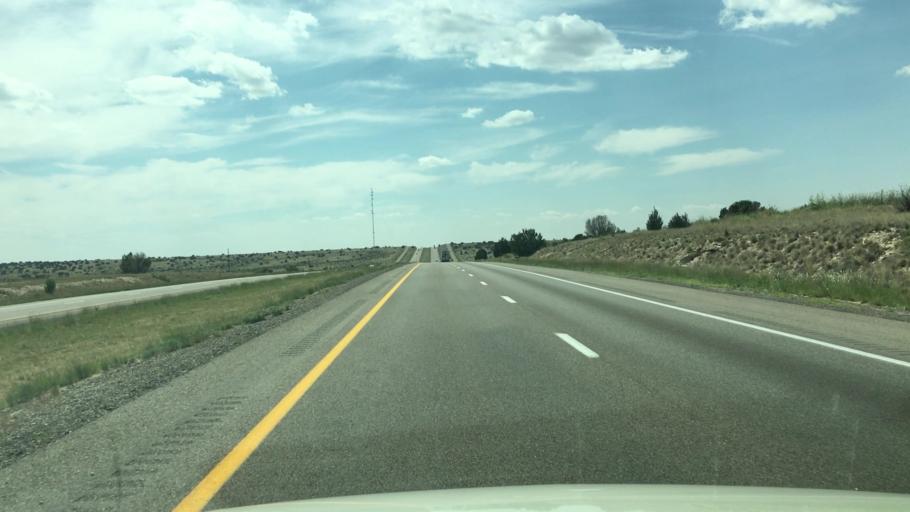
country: US
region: New Mexico
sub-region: Guadalupe County
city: Santa Rosa
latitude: 34.9713
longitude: -104.8899
